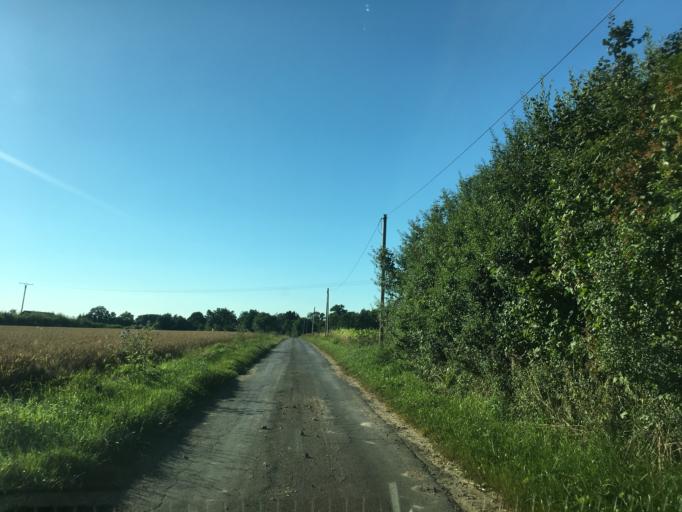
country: DE
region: North Rhine-Westphalia
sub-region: Regierungsbezirk Munster
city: Altenberge
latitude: 52.0203
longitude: 7.4843
